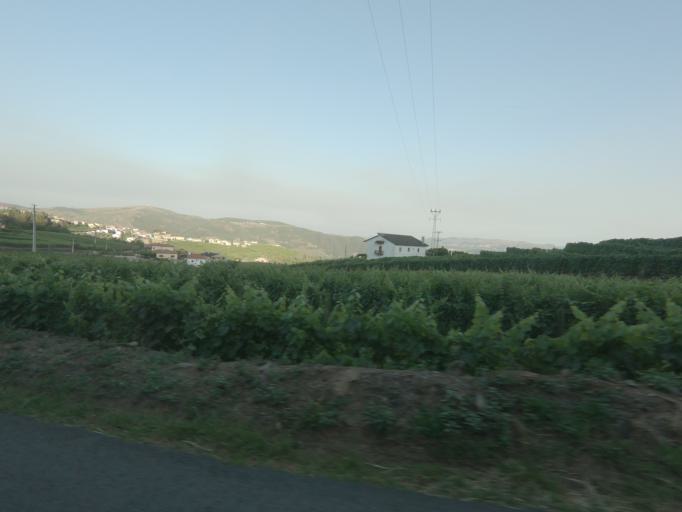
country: PT
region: Vila Real
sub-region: Sabrosa
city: Vilela
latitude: 41.2095
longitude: -7.6735
